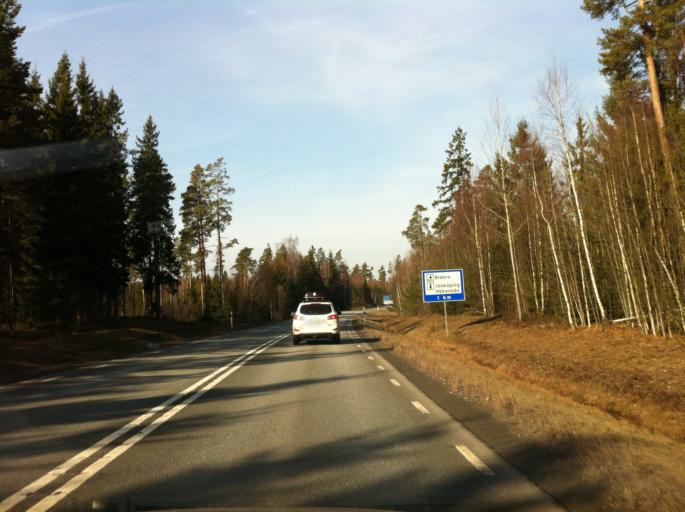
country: SE
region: Joenkoeping
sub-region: Habo Kommun
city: Habo
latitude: 57.8449
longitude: 14.0362
